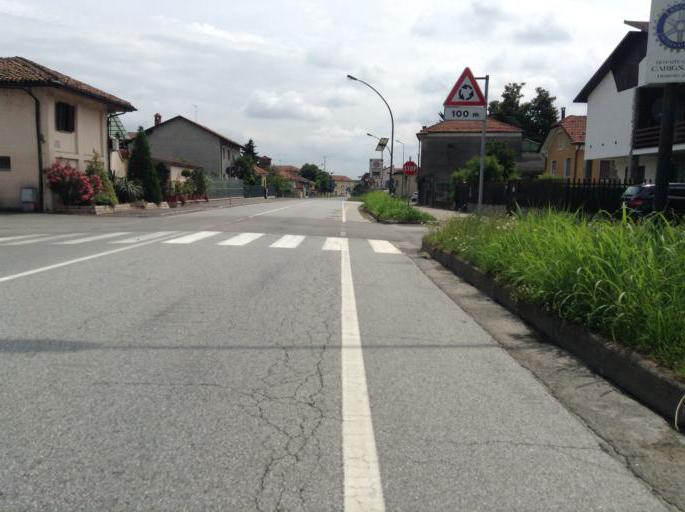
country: IT
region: Piedmont
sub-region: Provincia di Torino
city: Carignano
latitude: 44.9145
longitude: 7.6765
